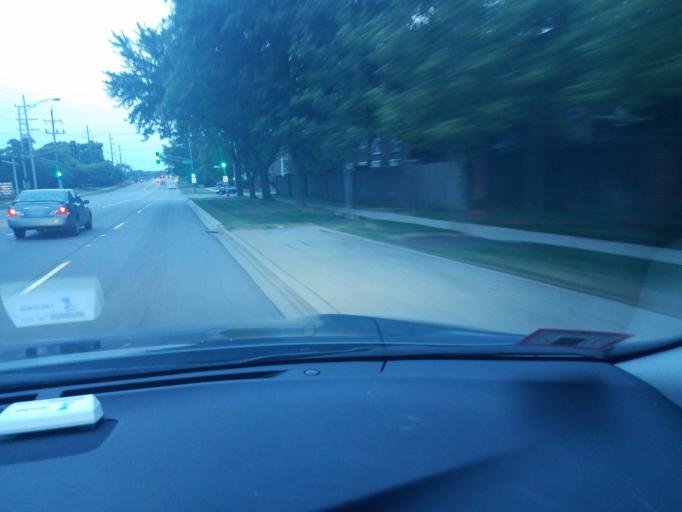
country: US
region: Illinois
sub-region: Cook County
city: Northbrook
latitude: 42.1379
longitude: -87.7976
